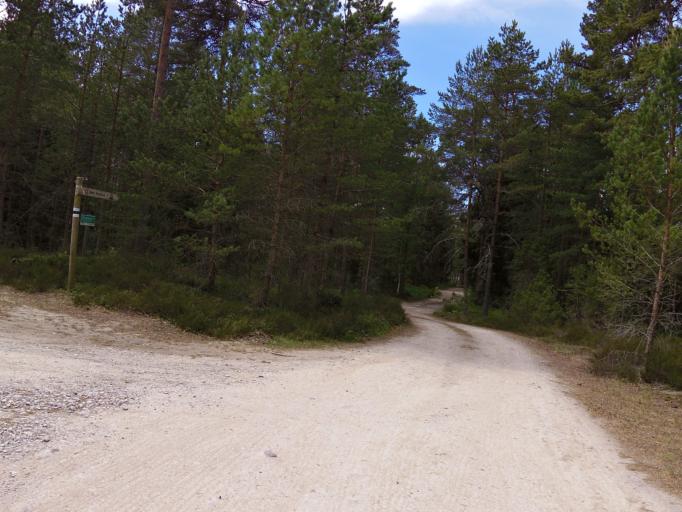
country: EE
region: Harju
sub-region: Paldiski linn
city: Paldiski
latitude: 59.2482
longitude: 23.7480
